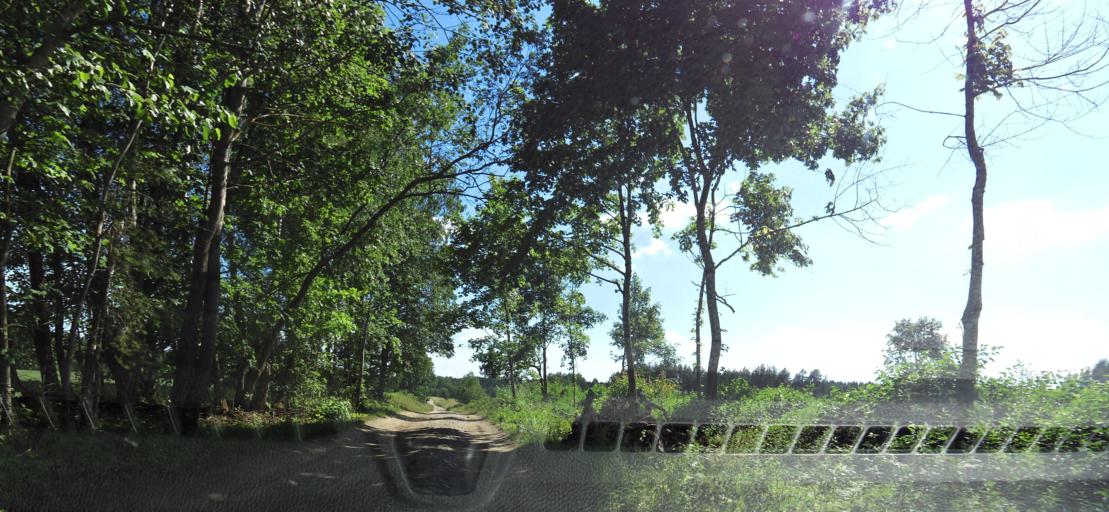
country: LT
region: Vilnius County
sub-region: Vilnius
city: Fabijoniskes
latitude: 54.8360
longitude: 25.3244
